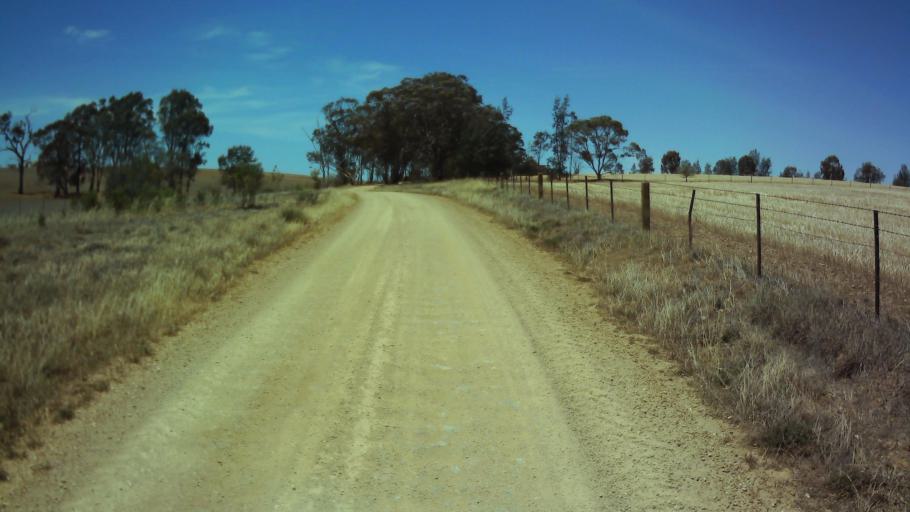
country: AU
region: New South Wales
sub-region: Weddin
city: Grenfell
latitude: -33.9287
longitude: 148.1700
